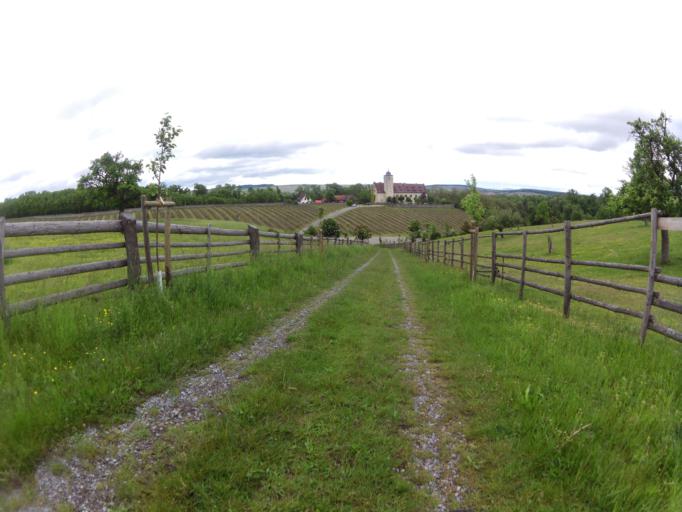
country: DE
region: Bavaria
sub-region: Regierungsbezirk Unterfranken
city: Sommerach
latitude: 49.8487
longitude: 10.2107
